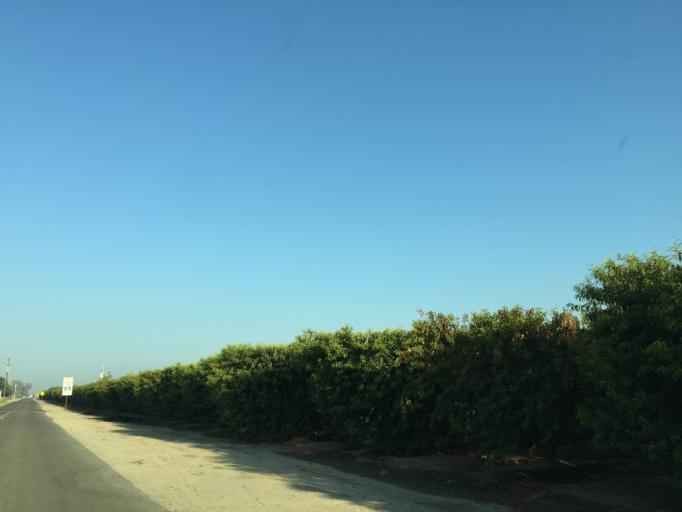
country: US
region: California
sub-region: Tulare County
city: London
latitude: 36.4590
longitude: -119.4770
